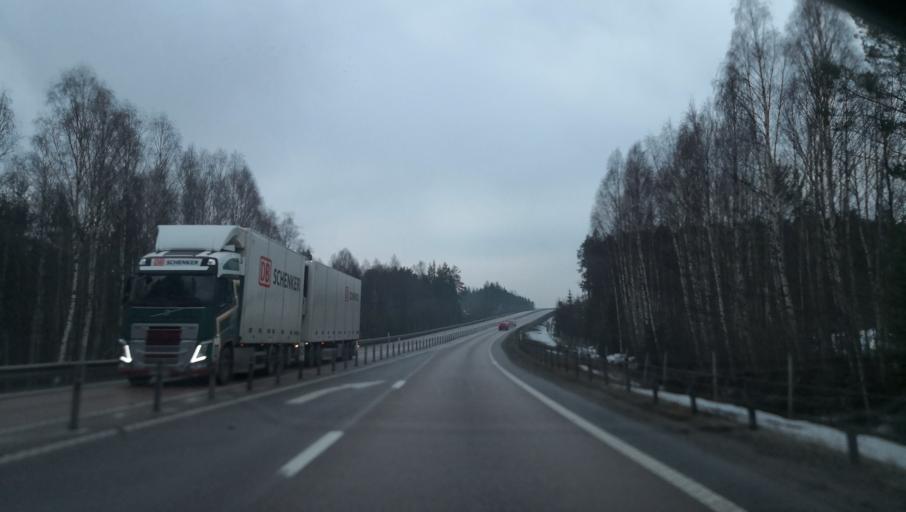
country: SE
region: Gaevleborg
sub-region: Nordanstigs Kommun
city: Bergsjoe
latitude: 61.8804
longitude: 17.1988
